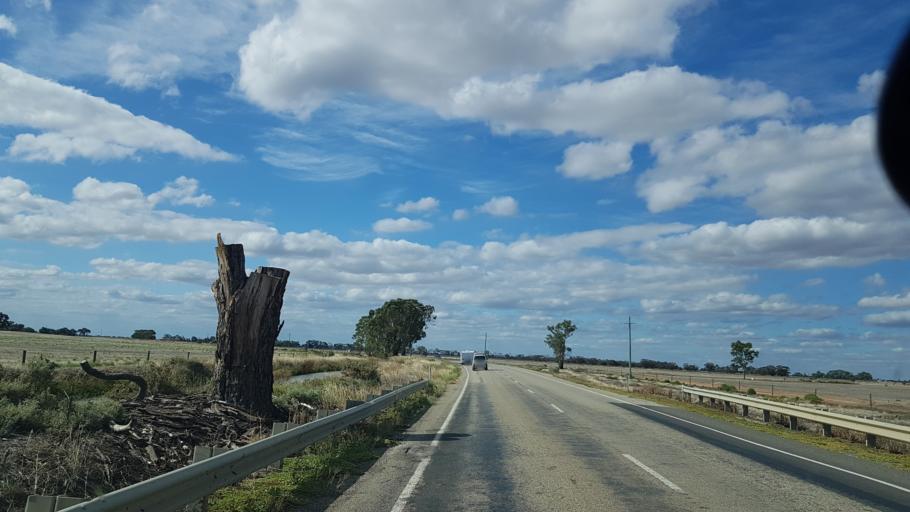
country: AU
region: Victoria
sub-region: Swan Hill
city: Swan Hill
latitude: -35.8140
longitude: 143.9548
